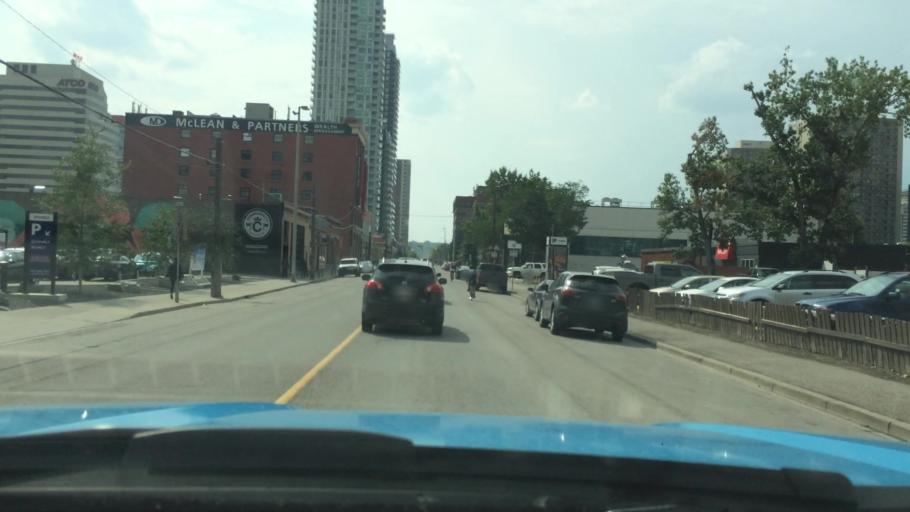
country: CA
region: Alberta
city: Calgary
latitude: 51.0438
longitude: -114.0771
